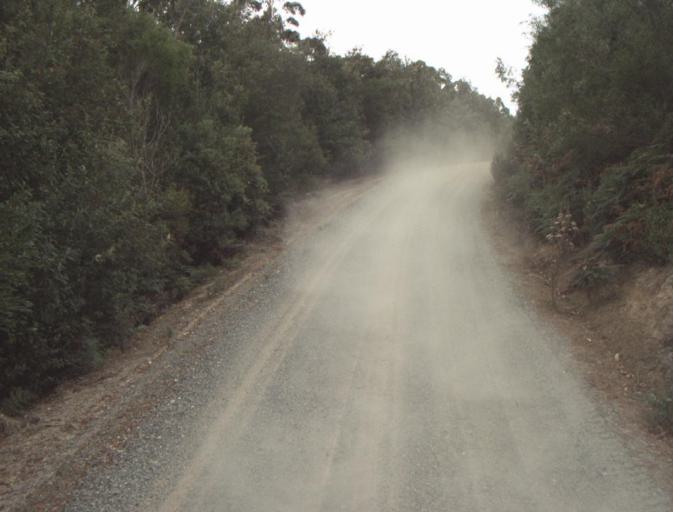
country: AU
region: Tasmania
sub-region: Launceston
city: Mayfield
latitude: -41.1606
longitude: 147.1748
